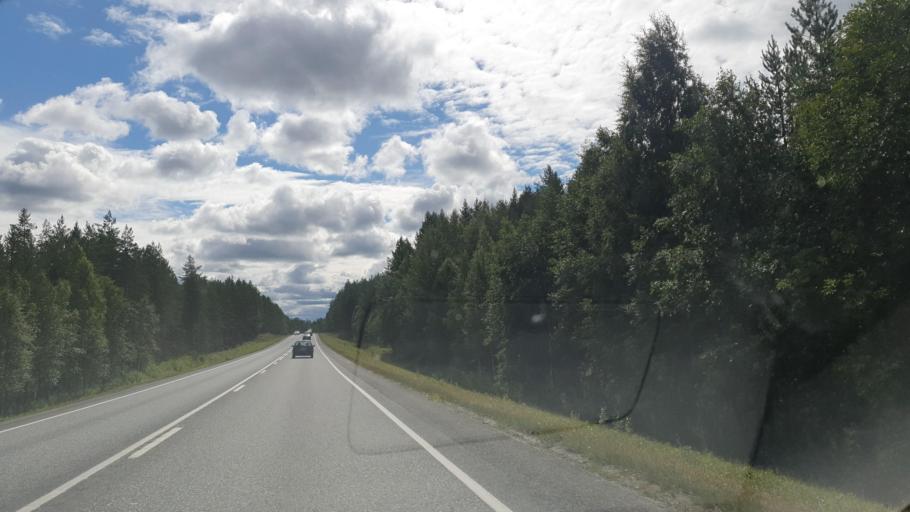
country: FI
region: Kainuu
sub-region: Kajaani
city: Kajaani
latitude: 64.1443
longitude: 27.5007
